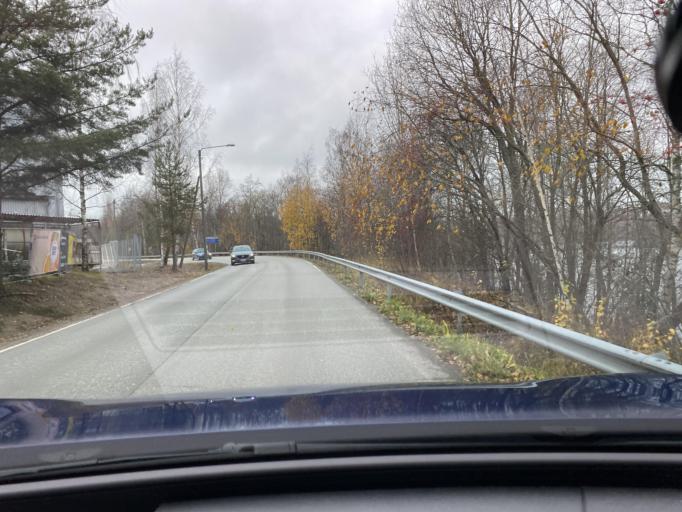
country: FI
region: Pirkanmaa
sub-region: Tampere
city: Nokia
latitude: 61.4699
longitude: 23.5220
